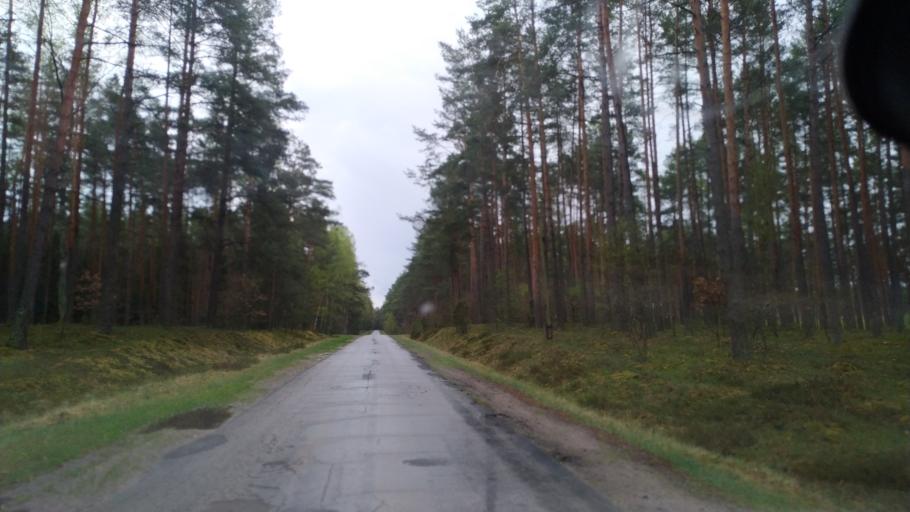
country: PL
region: Pomeranian Voivodeship
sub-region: Powiat starogardzki
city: Osiek
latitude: 53.6700
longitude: 18.4785
